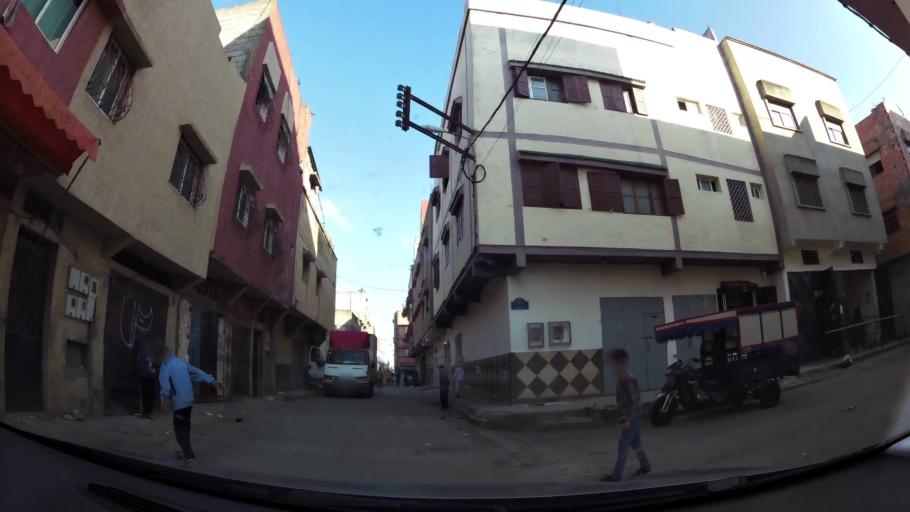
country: MA
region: Rabat-Sale-Zemmour-Zaer
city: Sale
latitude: 34.0606
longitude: -6.7879
